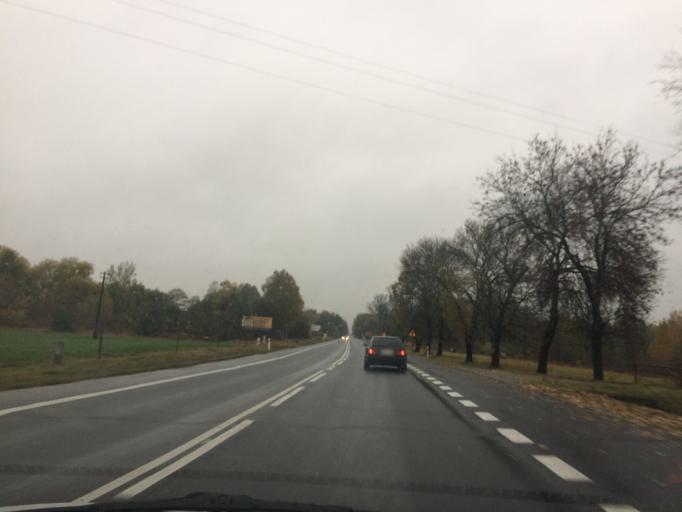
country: PL
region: Masovian Voivodeship
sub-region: Powiat otwocki
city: Kolbiel
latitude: 52.0765
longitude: 21.4470
